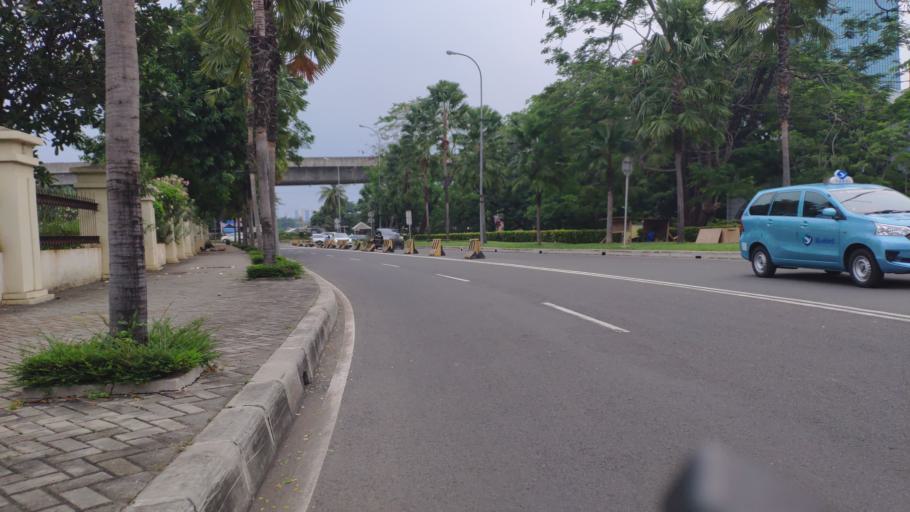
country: ID
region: Jakarta Raya
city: Jakarta
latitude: -6.2244
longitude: 106.8356
